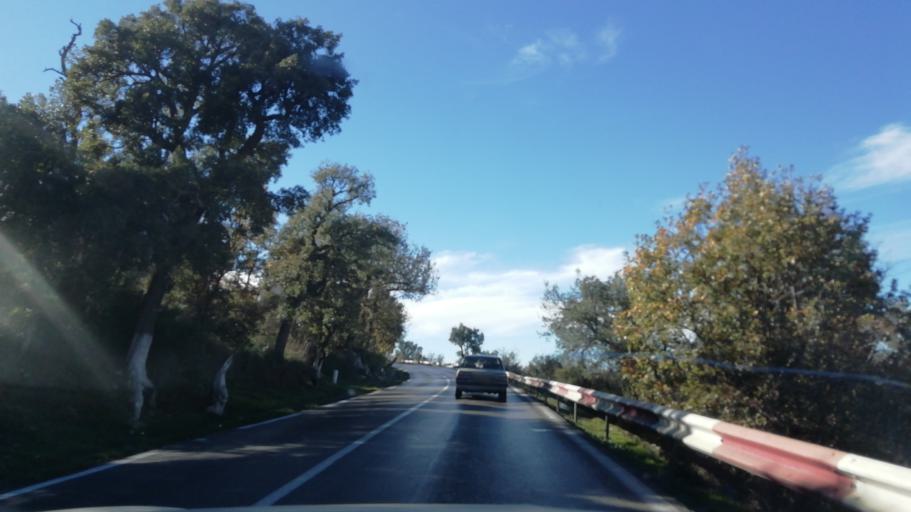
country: DZ
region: Tlemcen
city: Mansoura
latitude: 34.8429
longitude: -1.3650
